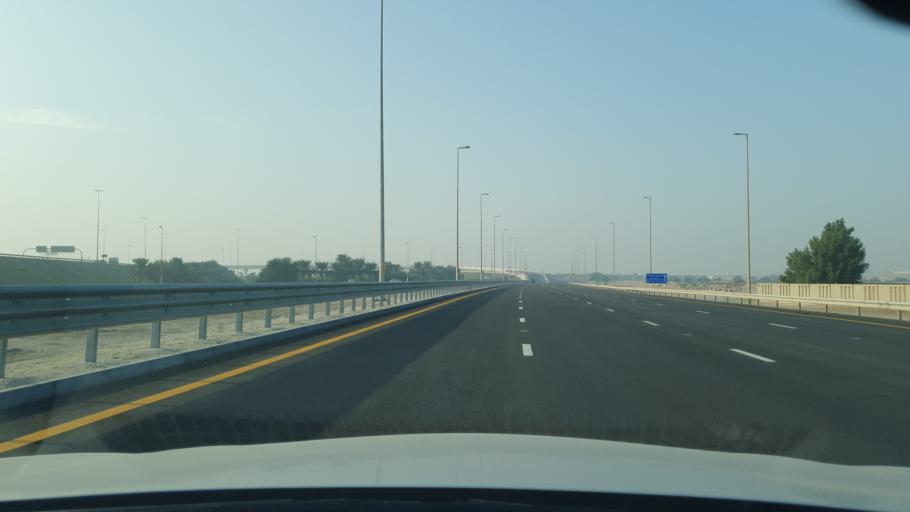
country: BH
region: Northern
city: Madinat `Isa
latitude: 26.1889
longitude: 50.5033
